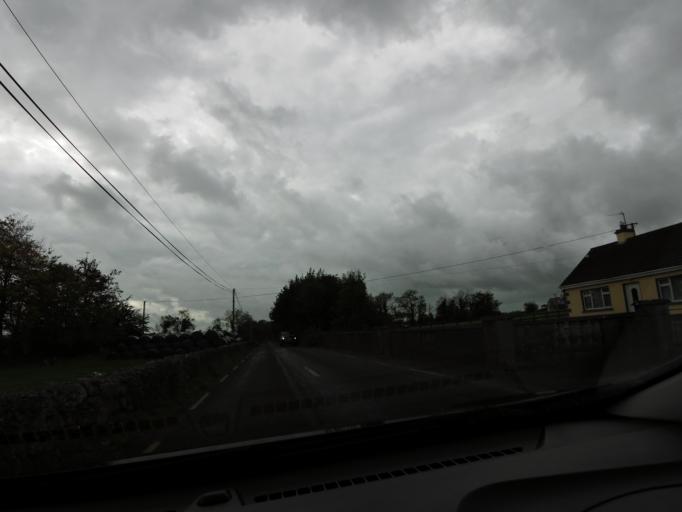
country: IE
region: Connaught
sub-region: County Galway
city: Loughrea
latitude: 53.2856
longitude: -8.6000
